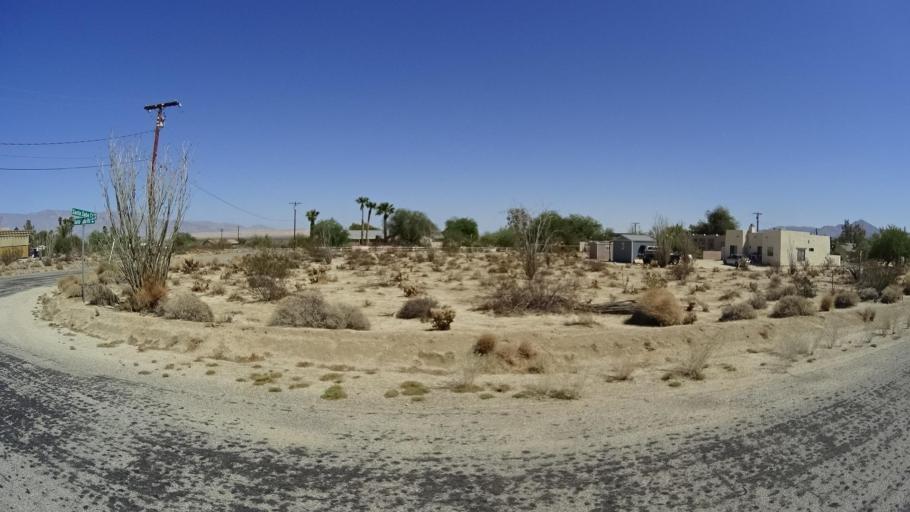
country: US
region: California
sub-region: San Diego County
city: Borrego Springs
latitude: 33.2216
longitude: -116.3677
